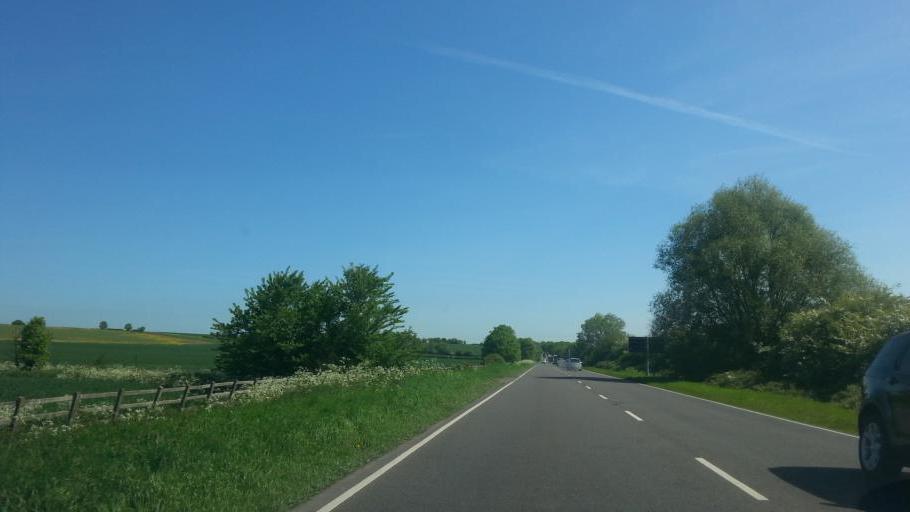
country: GB
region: England
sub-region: Cambridgeshire
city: Godmanchester
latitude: 52.3424
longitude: -0.1488
